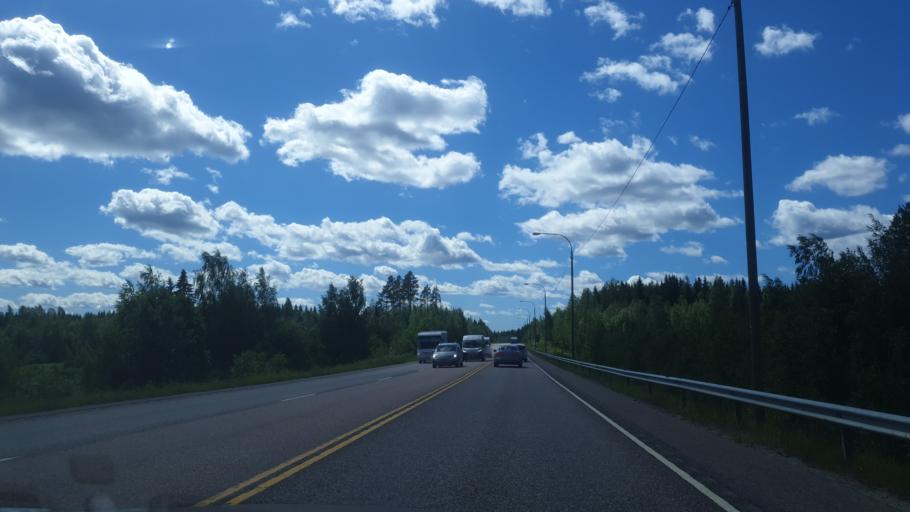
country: FI
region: Northern Savo
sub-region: Varkaus
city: Varkaus
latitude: 62.3944
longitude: 27.8177
